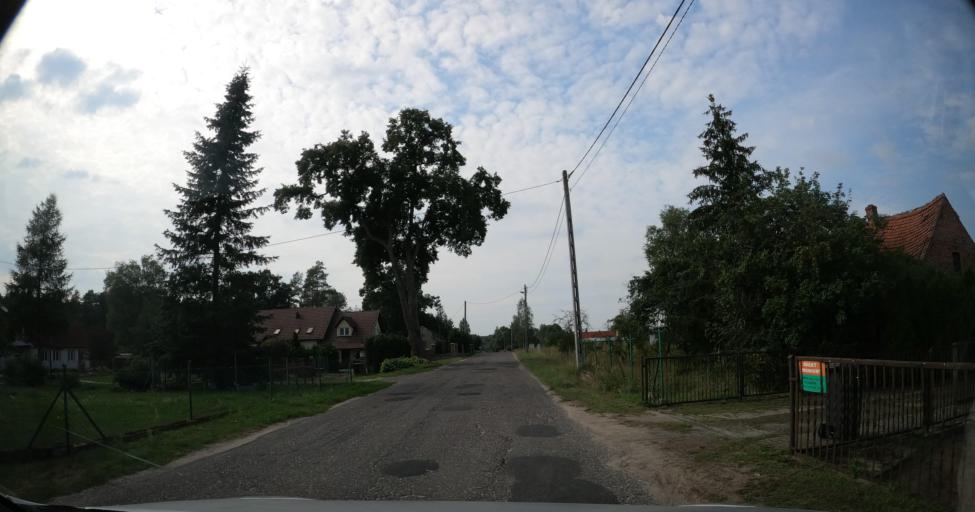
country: PL
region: West Pomeranian Voivodeship
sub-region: Powiat goleniowski
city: Goleniow
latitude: 53.5049
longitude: 14.8750
